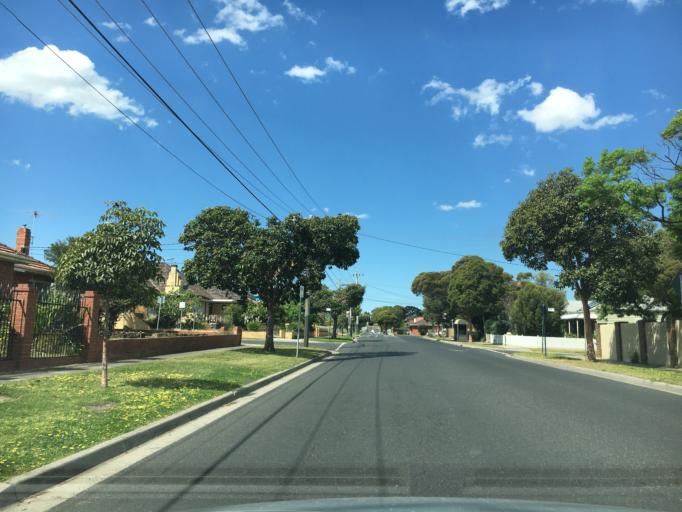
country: AU
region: Victoria
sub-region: Monash
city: Chadstone
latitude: -37.9034
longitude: 145.1035
